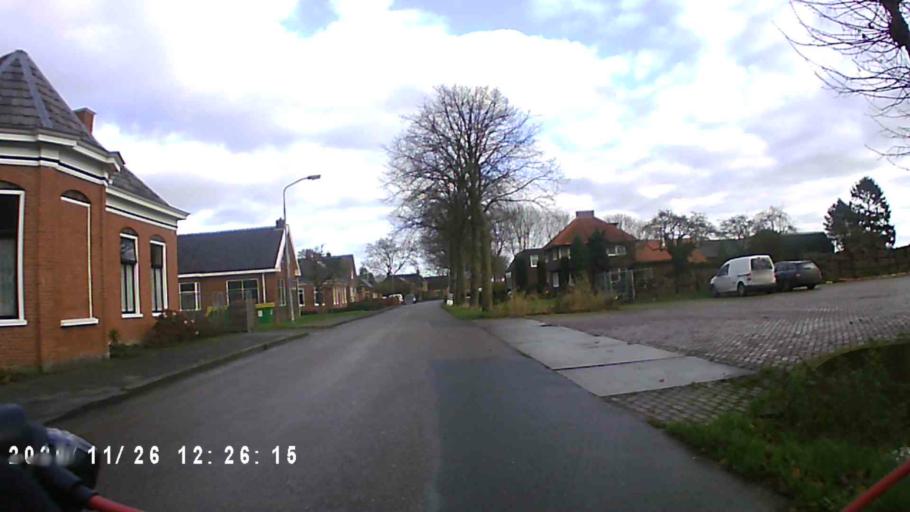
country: NL
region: Groningen
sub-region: Gemeente Bedum
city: Bedum
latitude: 53.3222
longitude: 6.6987
